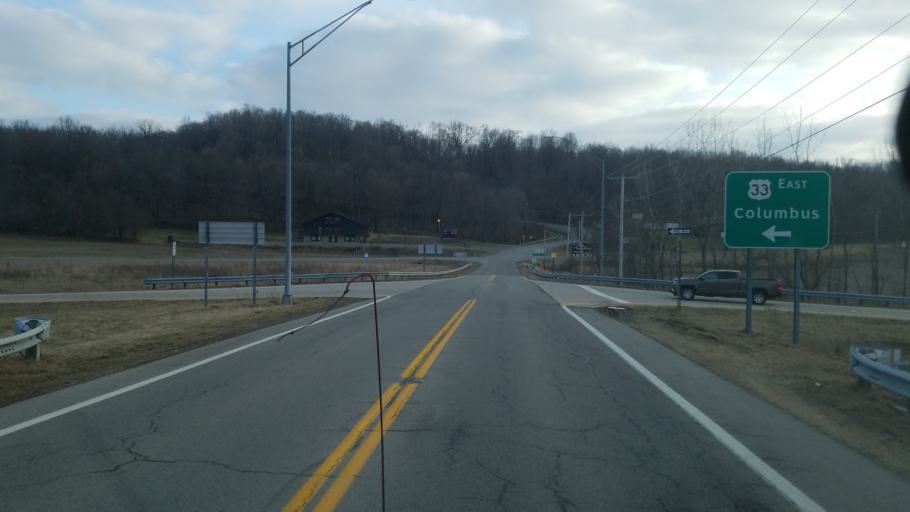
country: US
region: Ohio
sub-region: Logan County
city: Bellefontaine
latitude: 40.3244
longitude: -83.6635
